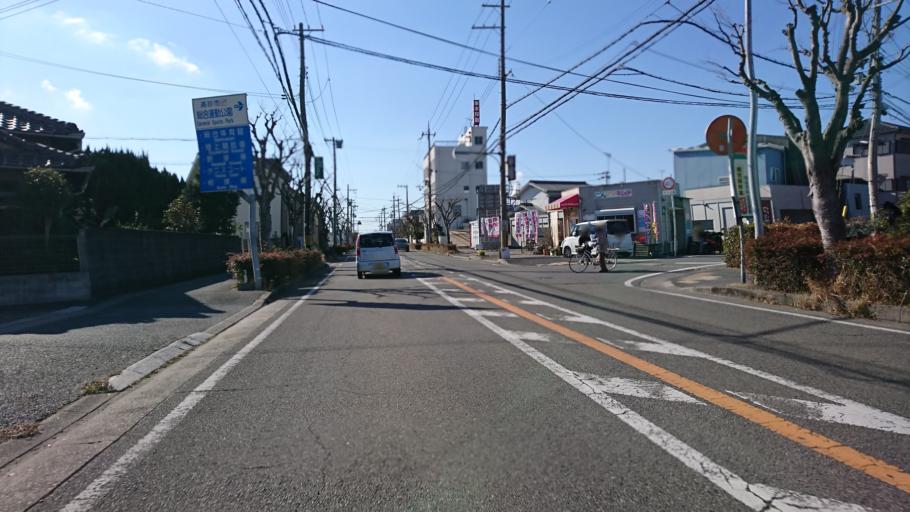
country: JP
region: Hyogo
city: Kakogawacho-honmachi
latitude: 34.7778
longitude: 134.8058
